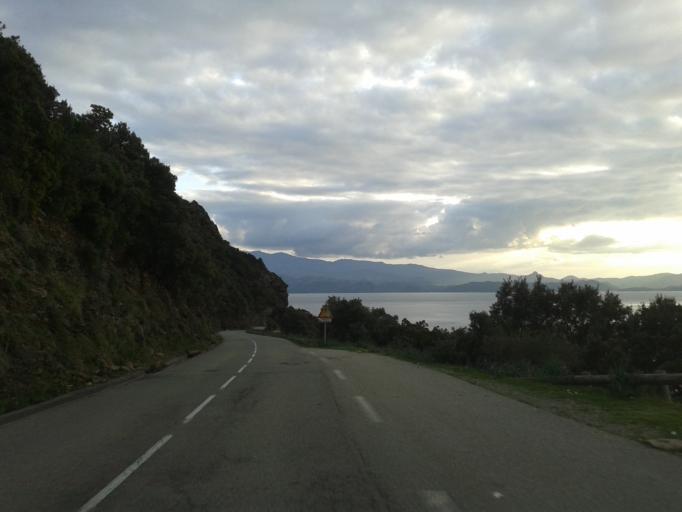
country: FR
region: Corsica
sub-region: Departement de la Haute-Corse
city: Saint-Florent
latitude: 42.7667
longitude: 9.3397
